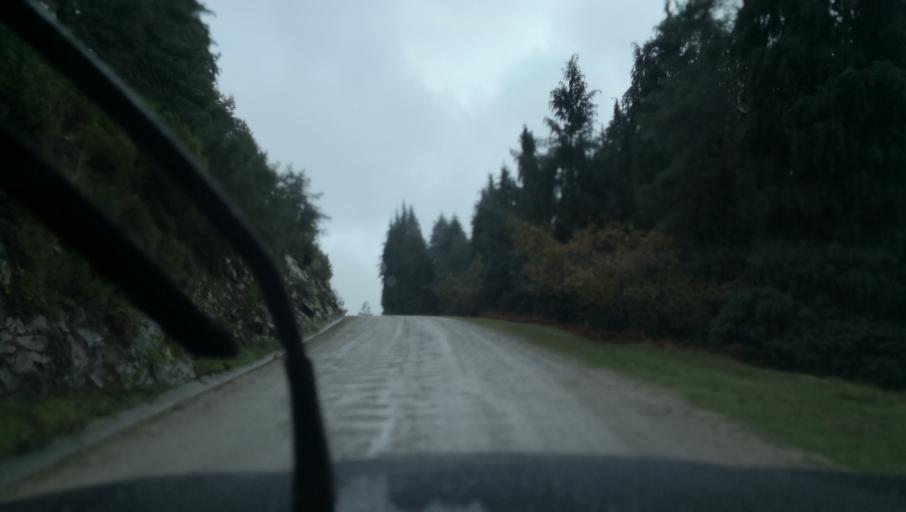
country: PT
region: Vila Real
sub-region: Mondim de Basto
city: Mondim de Basto
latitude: 41.3210
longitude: -7.8746
